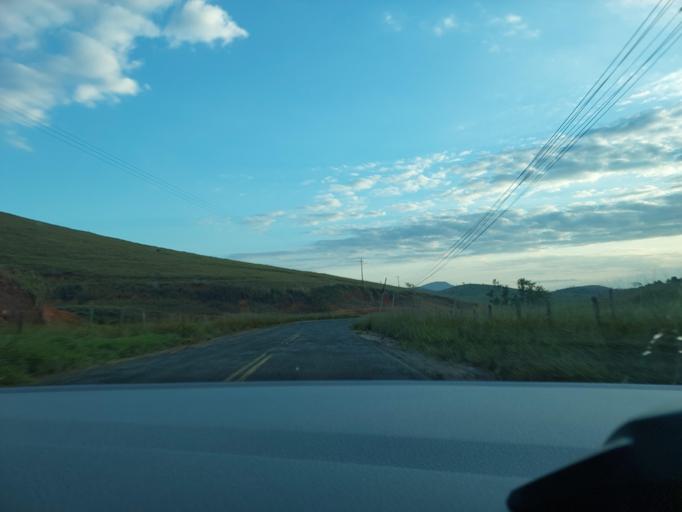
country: BR
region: Rio de Janeiro
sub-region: Natividade
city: Natividade
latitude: -21.1917
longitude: -42.1125
